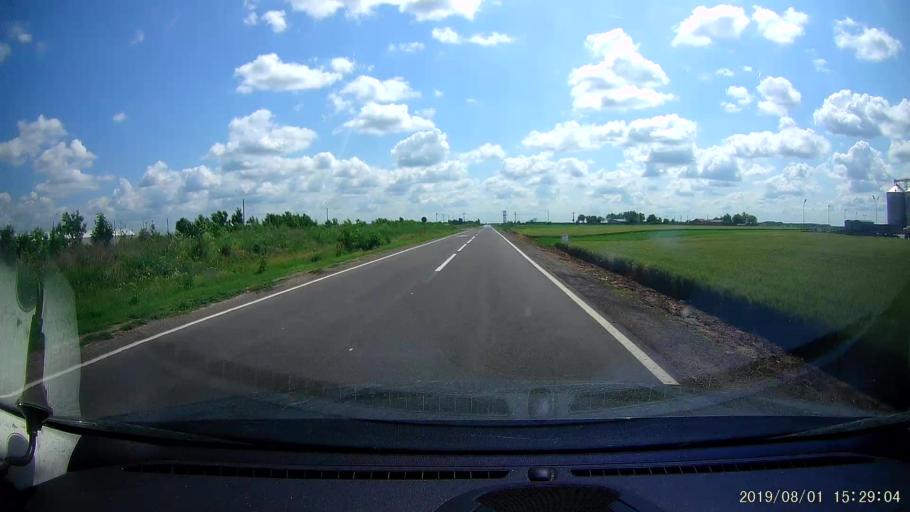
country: RO
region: Braila
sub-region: Comuna Viziru
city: Viziru
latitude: 44.9879
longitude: 27.7031
